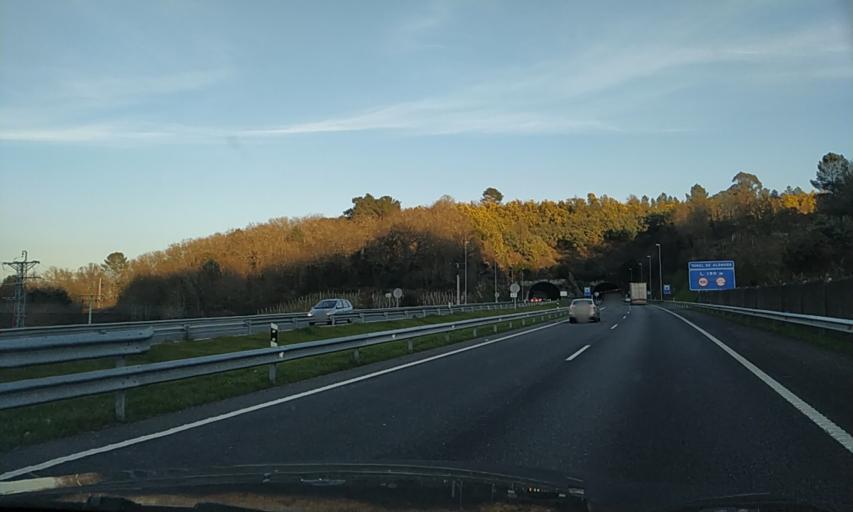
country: ES
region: Galicia
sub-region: Provincia de Ourense
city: Toen
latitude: 42.3315
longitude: -7.9611
